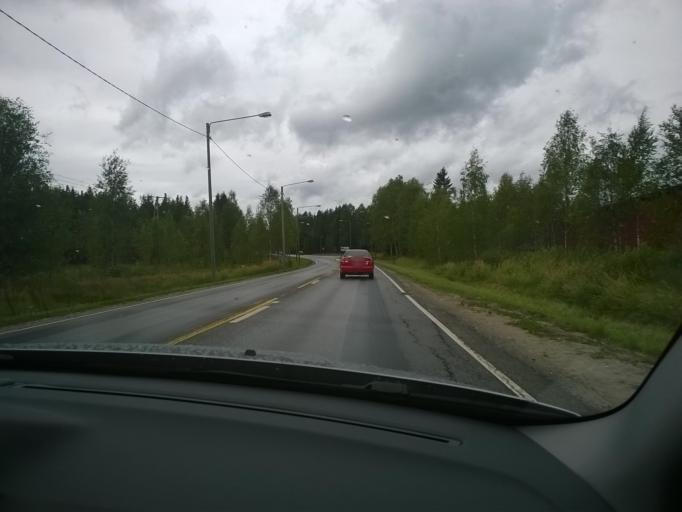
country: FI
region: Kainuu
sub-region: Kehys-Kainuu
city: Kuhmo
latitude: 64.1308
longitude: 29.4840
